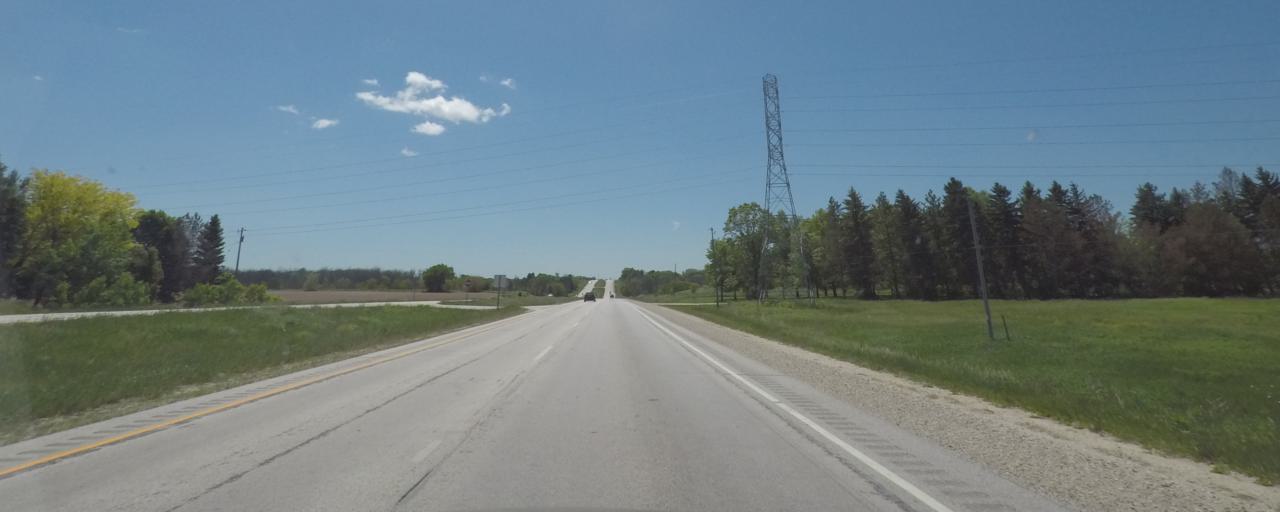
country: US
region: Wisconsin
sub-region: Sheboygan County
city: Plymouth
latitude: 43.7285
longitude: -87.9412
